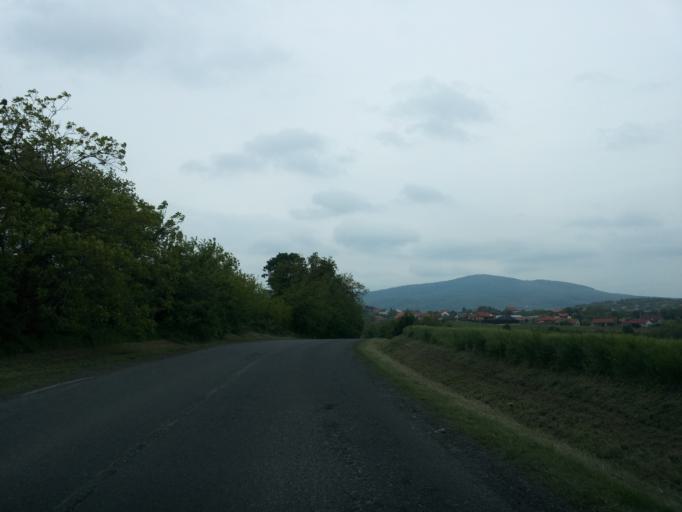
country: HU
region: Baranya
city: Hosszuheteny
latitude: 46.1399
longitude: 18.3478
